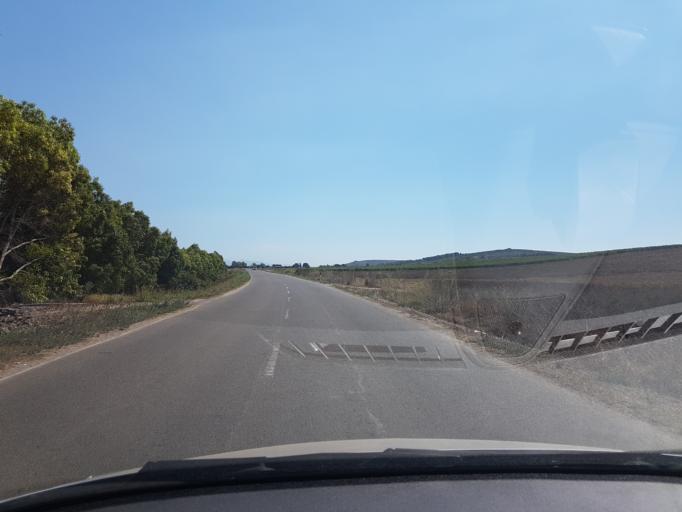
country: IT
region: Sardinia
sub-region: Provincia di Oristano
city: Nurachi
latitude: 39.9667
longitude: 8.4530
